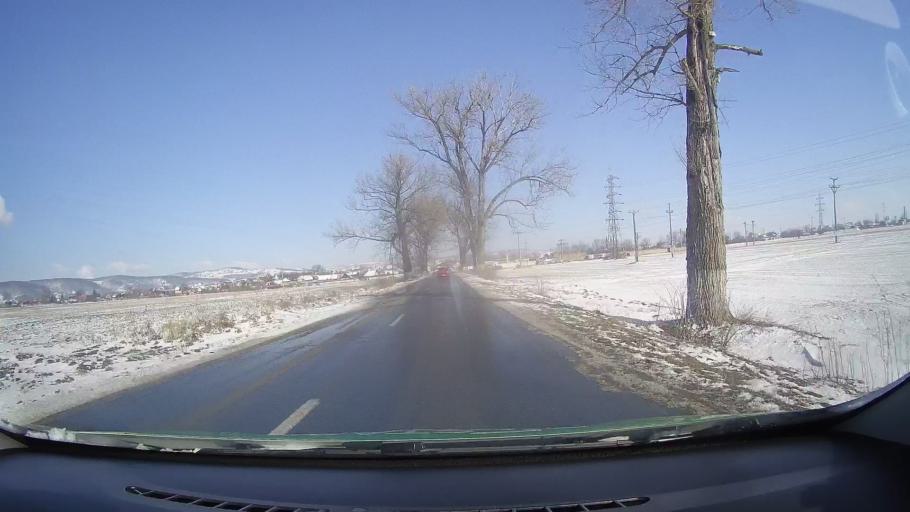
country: RO
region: Sibiu
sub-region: Comuna Avrig
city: Avrig
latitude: 45.7167
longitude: 24.3731
